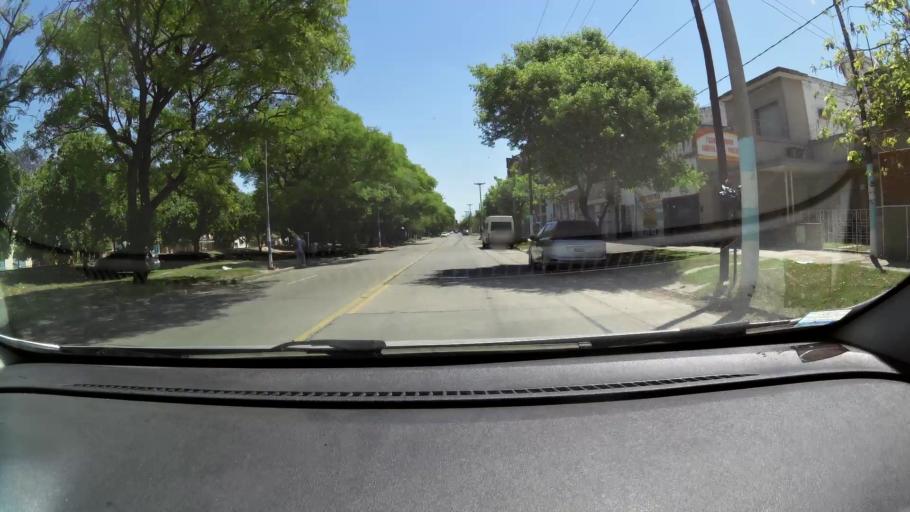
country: AR
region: Cordoba
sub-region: Departamento de Capital
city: Cordoba
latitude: -31.3942
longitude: -64.1552
